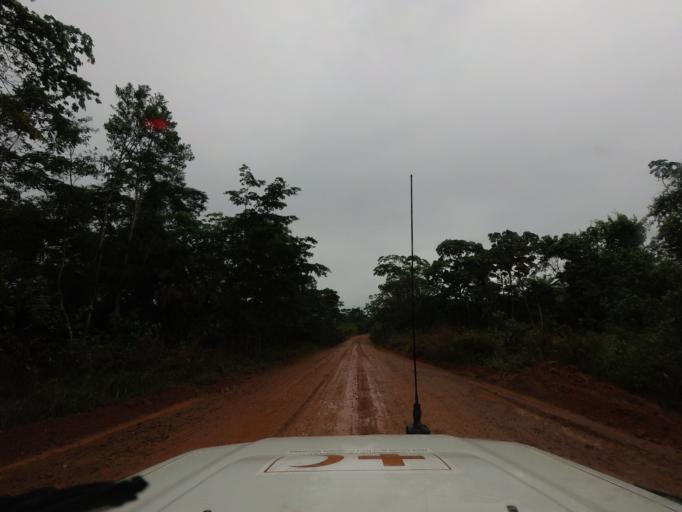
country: LR
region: Nimba
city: New Yekepa
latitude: 7.5182
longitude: -8.5962
